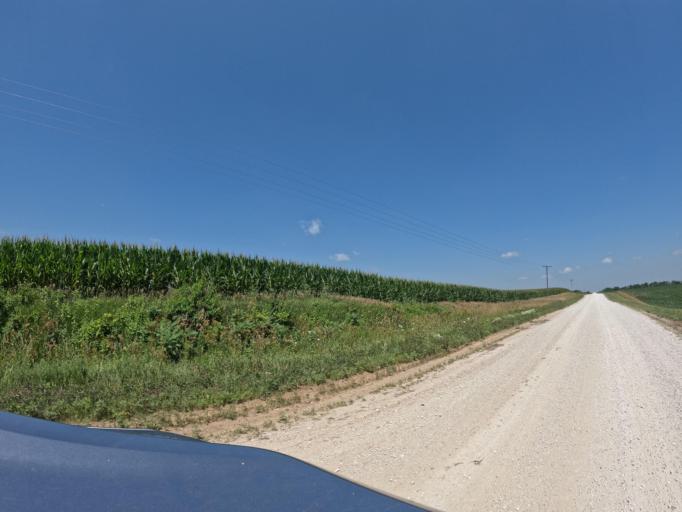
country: US
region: Iowa
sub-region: Keokuk County
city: Sigourney
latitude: 41.2760
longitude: -92.2381
